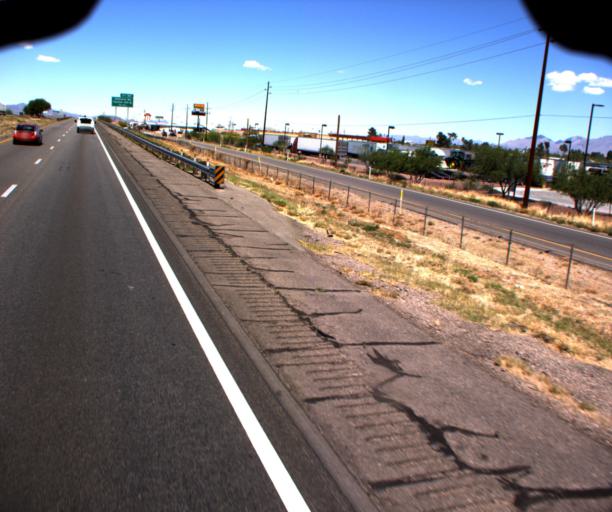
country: US
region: Arizona
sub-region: Pima County
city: Summit
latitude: 32.1238
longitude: -110.8725
